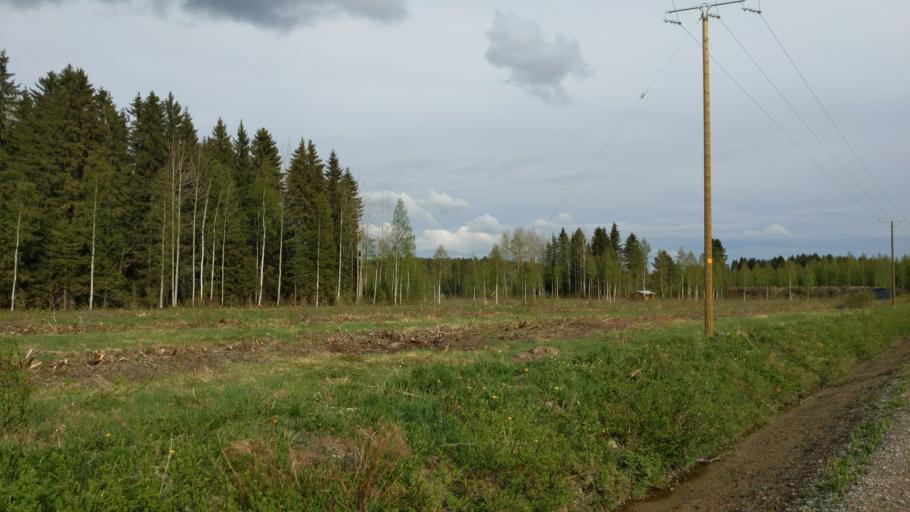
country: FI
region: Northern Savo
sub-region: Ylae-Savo
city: Iisalmi
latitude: 63.5882
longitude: 27.0348
